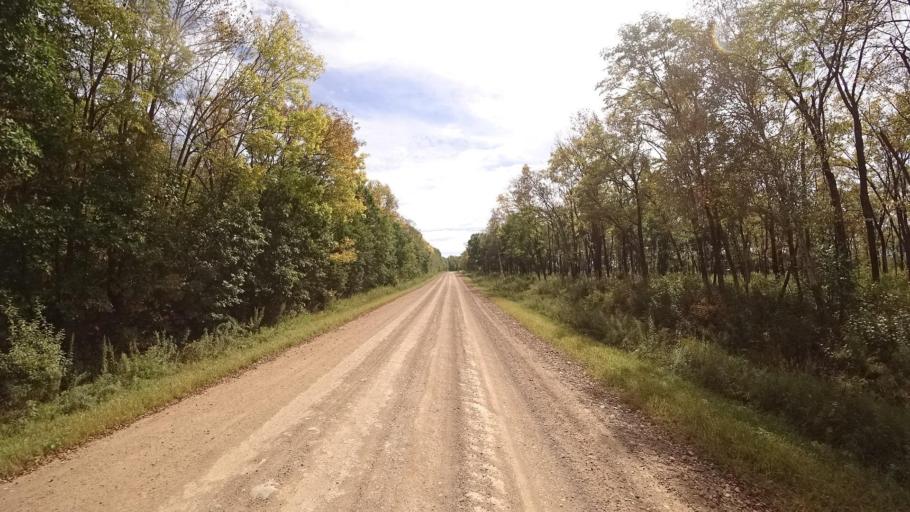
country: RU
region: Primorskiy
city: Yakovlevka
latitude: 44.6333
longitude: 133.6006
